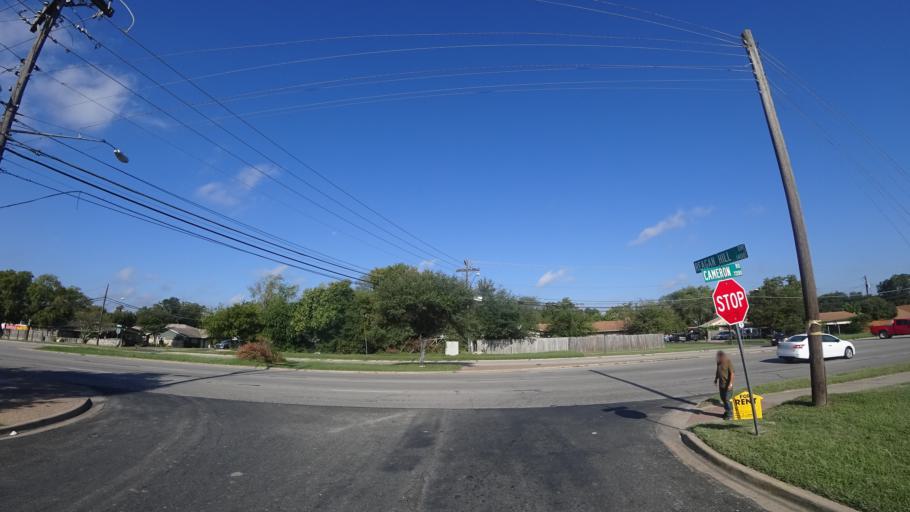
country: US
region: Texas
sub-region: Travis County
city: Austin
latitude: 30.3273
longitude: -97.6912
